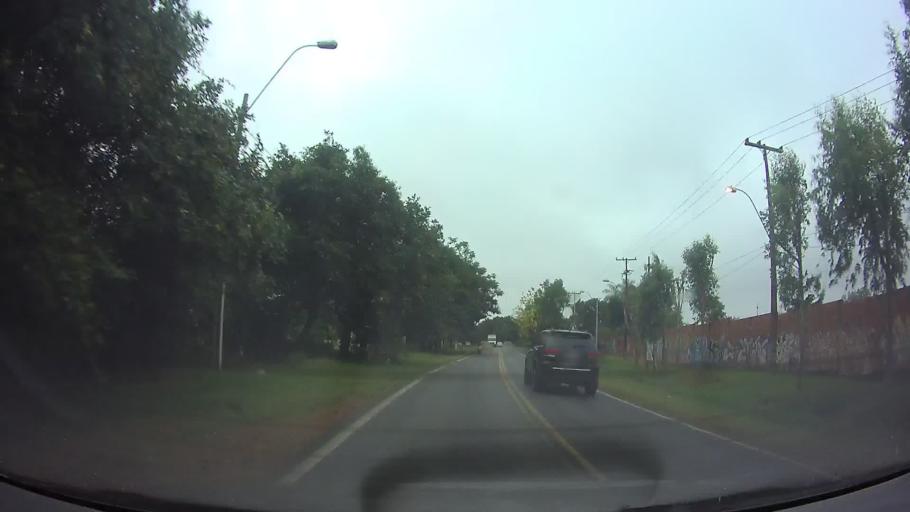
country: PY
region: Central
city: Itaugua
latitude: -25.3979
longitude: -57.3577
